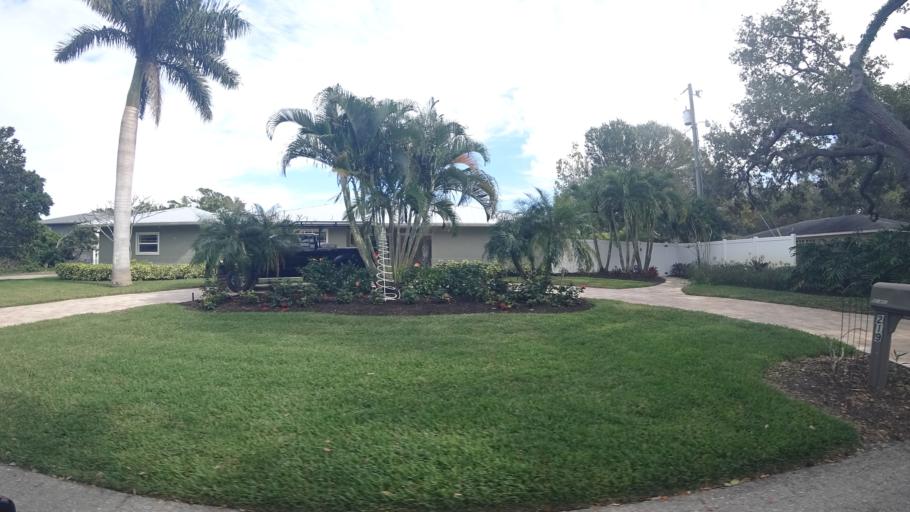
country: US
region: Florida
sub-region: Manatee County
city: West Bradenton
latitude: 27.4985
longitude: -82.6429
